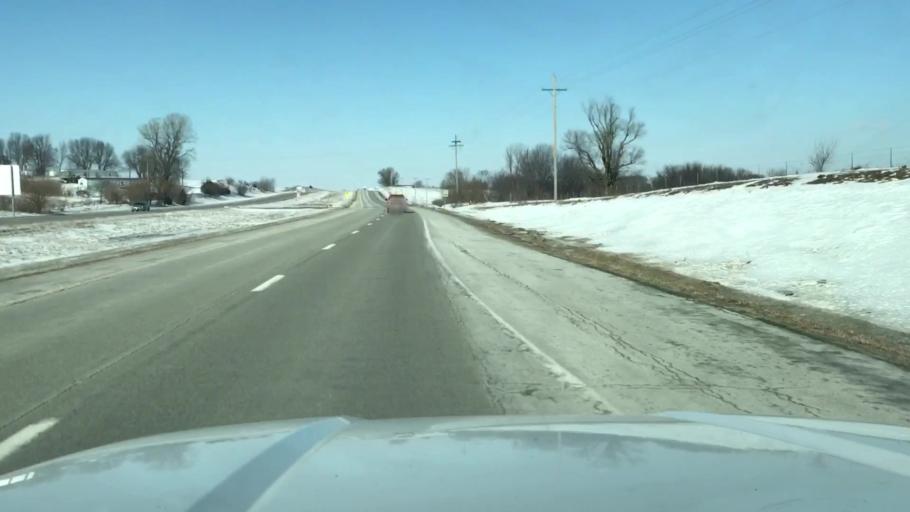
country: US
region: Missouri
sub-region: Andrew County
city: Savannah
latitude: 39.9654
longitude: -94.8652
